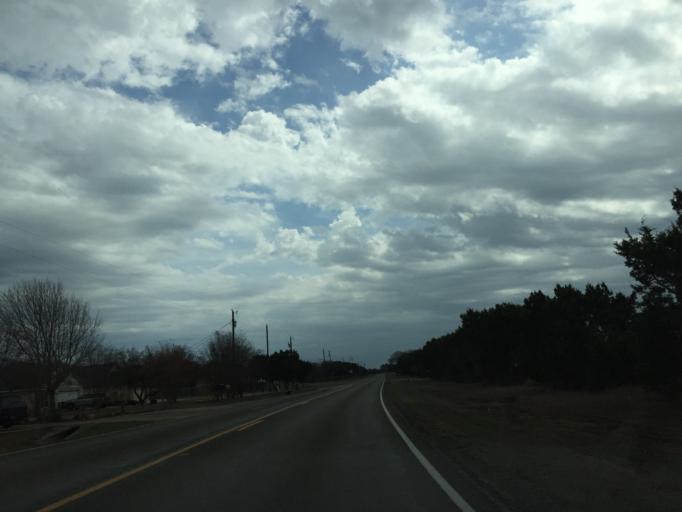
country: US
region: Texas
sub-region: Burnet County
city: Bertram
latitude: 30.6561
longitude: -98.0088
